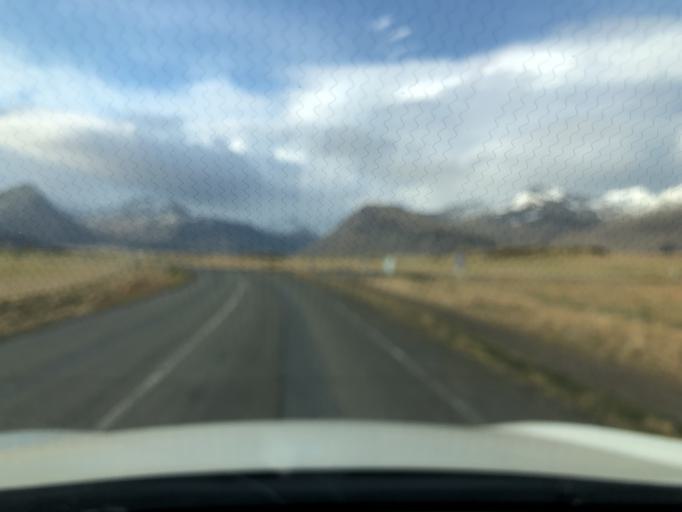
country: IS
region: East
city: Hoefn
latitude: 64.2888
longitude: -15.1828
